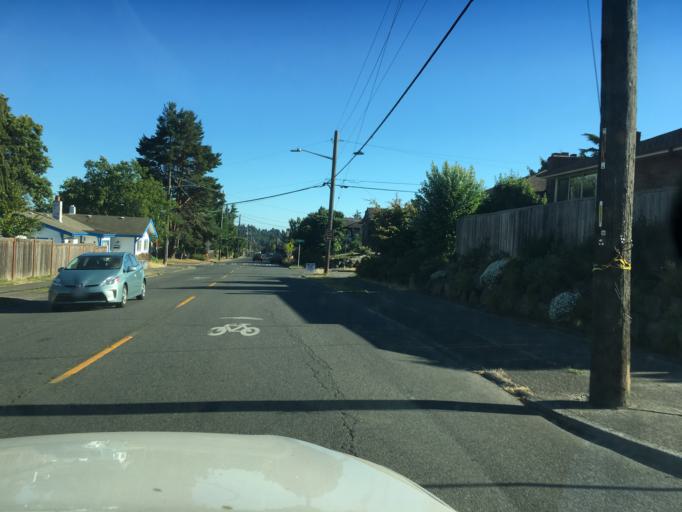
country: US
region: Washington
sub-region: King County
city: Shoreline
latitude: 47.6788
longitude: -122.3984
